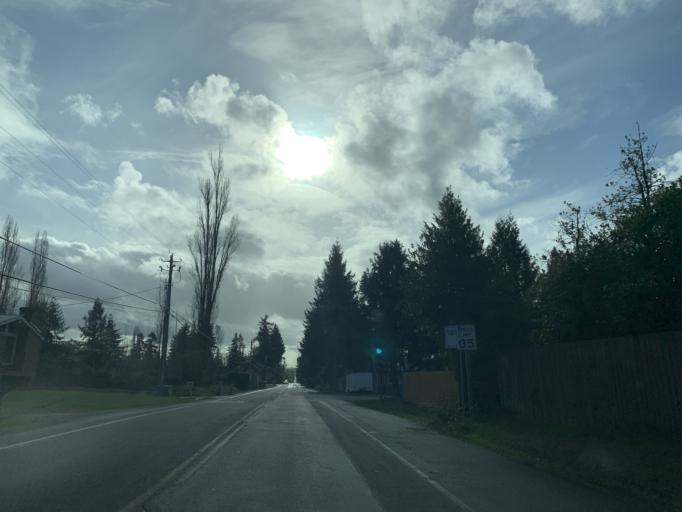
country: US
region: Washington
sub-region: King County
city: Lakeland South
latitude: 47.2736
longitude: -122.2978
